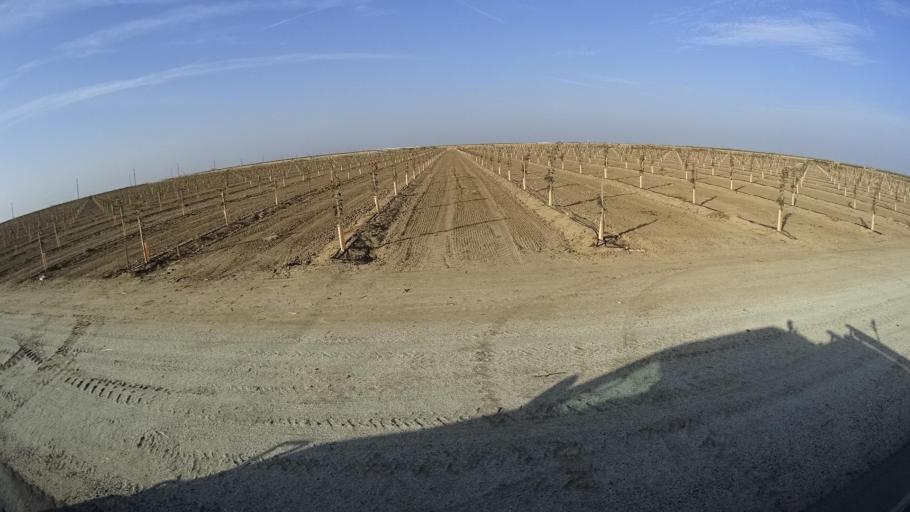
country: US
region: California
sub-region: Kern County
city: McFarland
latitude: 35.7065
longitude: -119.1871
